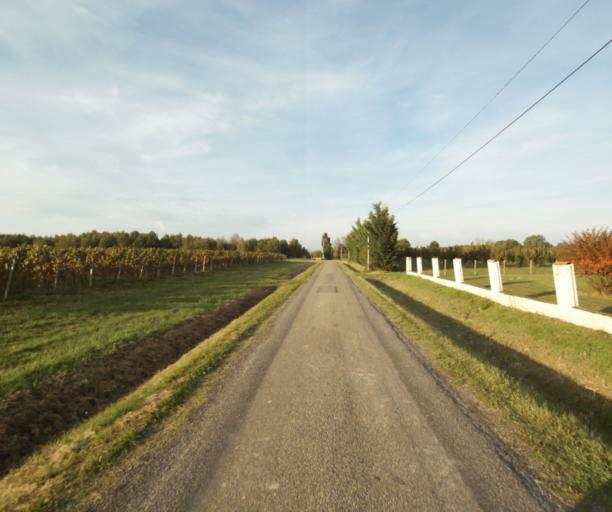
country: FR
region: Midi-Pyrenees
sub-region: Departement du Tarn-et-Garonne
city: Campsas
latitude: 43.8910
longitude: 1.3464
